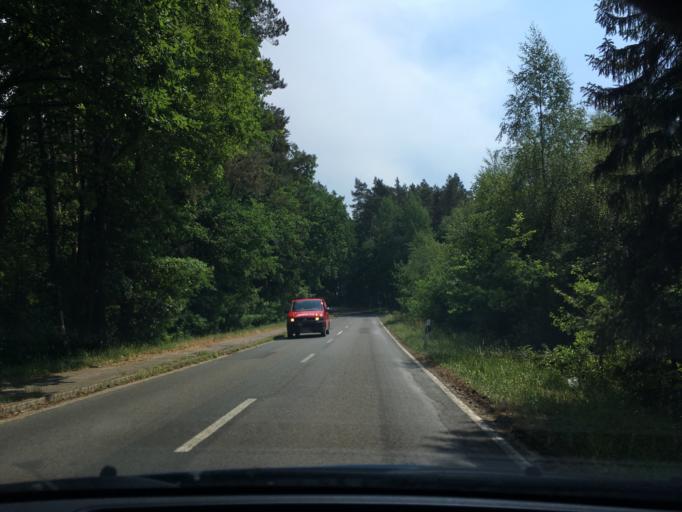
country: DE
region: Lower Saxony
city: Jesteburg
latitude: 53.2794
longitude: 9.9139
